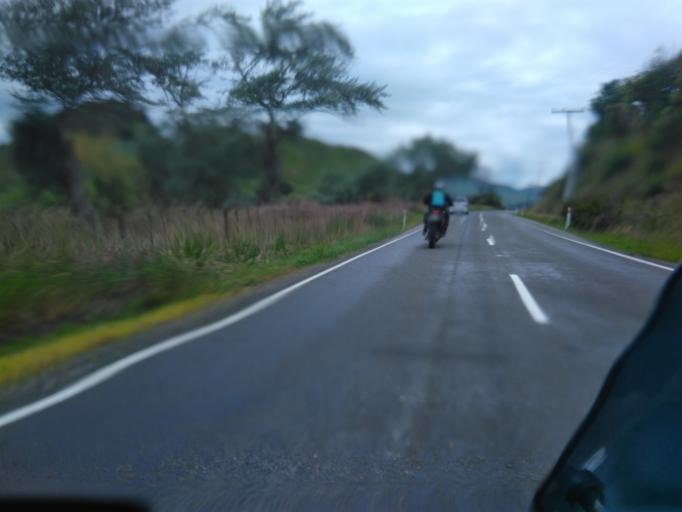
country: NZ
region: Bay of Plenty
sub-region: Opotiki District
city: Opotiki
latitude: -38.3621
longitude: 177.5009
